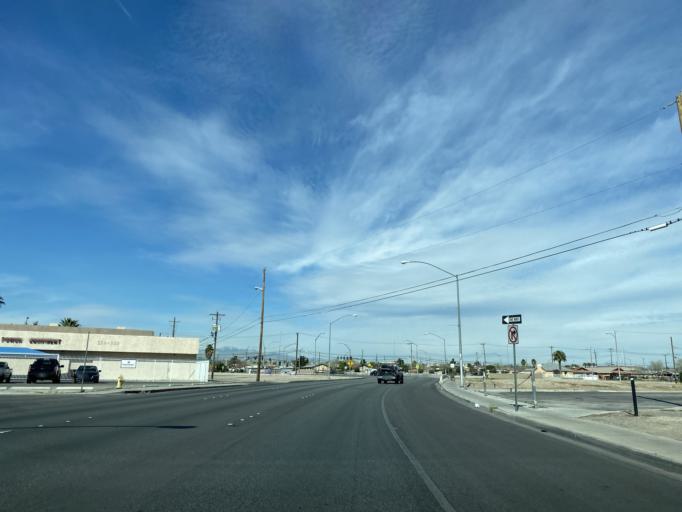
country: US
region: Nevada
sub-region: Clark County
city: North Las Vegas
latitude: 36.1962
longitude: -115.1317
